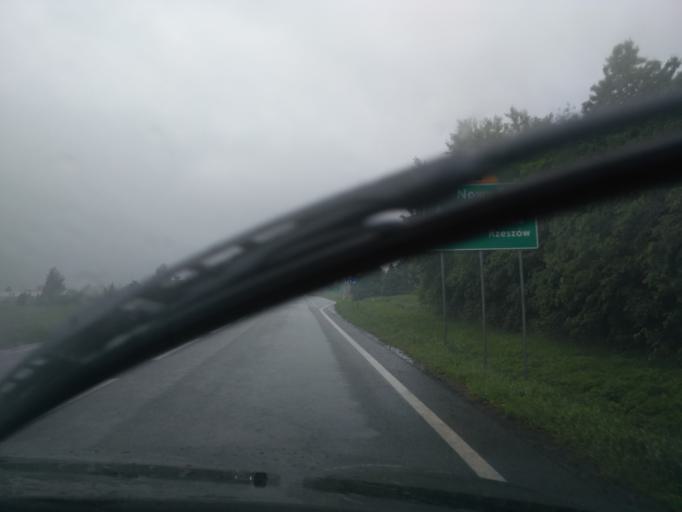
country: PL
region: Subcarpathian Voivodeship
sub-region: Powiat jasielski
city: Tarnowiec
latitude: 49.7612
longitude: 21.5471
